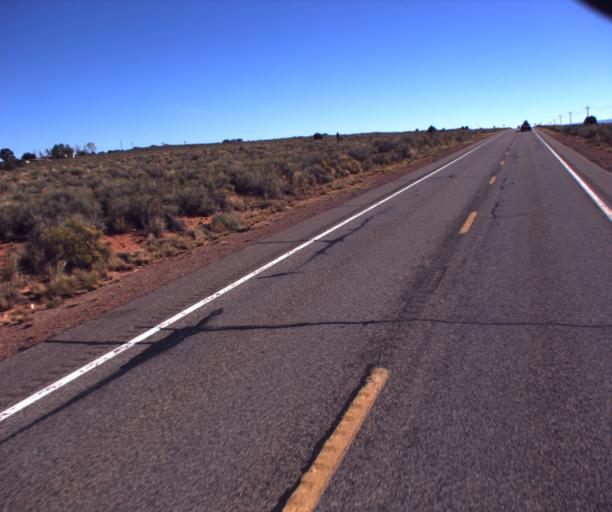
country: US
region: Arizona
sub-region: Coconino County
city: Fredonia
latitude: 36.8577
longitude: -112.7443
